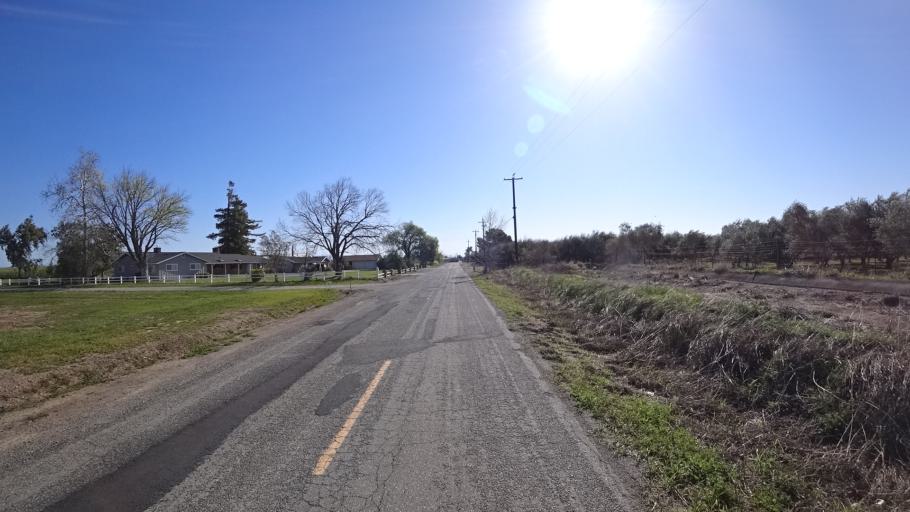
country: US
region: California
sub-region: Glenn County
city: Orland
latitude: 39.7476
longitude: -122.2193
